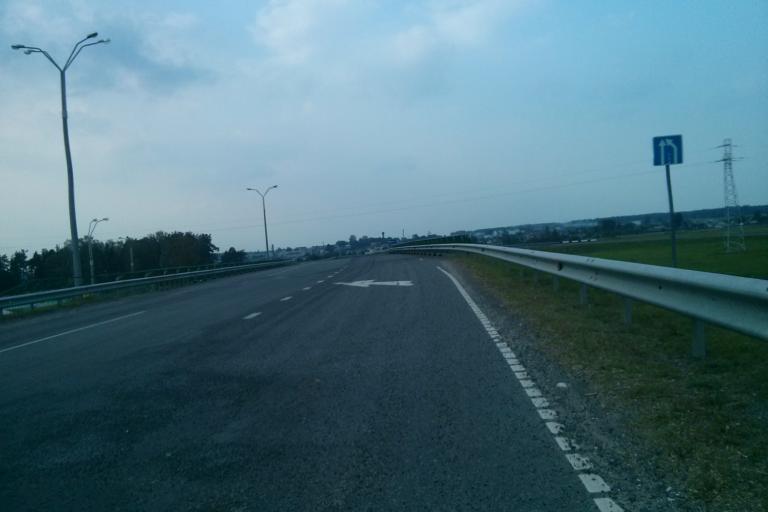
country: BY
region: Minsk
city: Chervyen'
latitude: 53.7235
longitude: 28.3946
